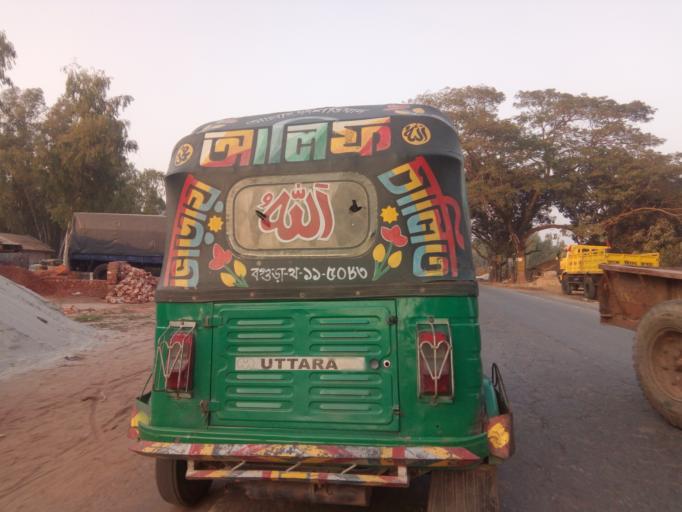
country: BD
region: Rajshahi
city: Bogra
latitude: 24.5940
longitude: 89.2369
